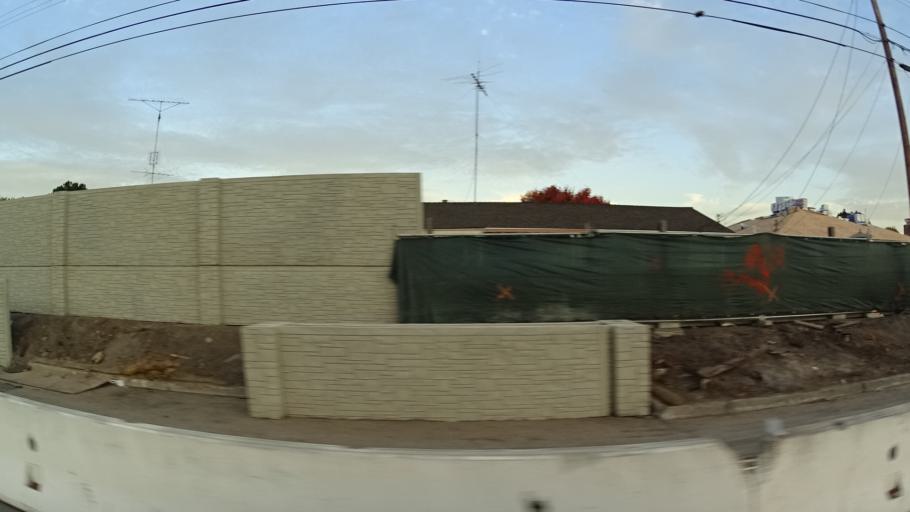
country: US
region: California
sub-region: Santa Clara County
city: Santa Clara
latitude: 37.3502
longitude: -121.9682
